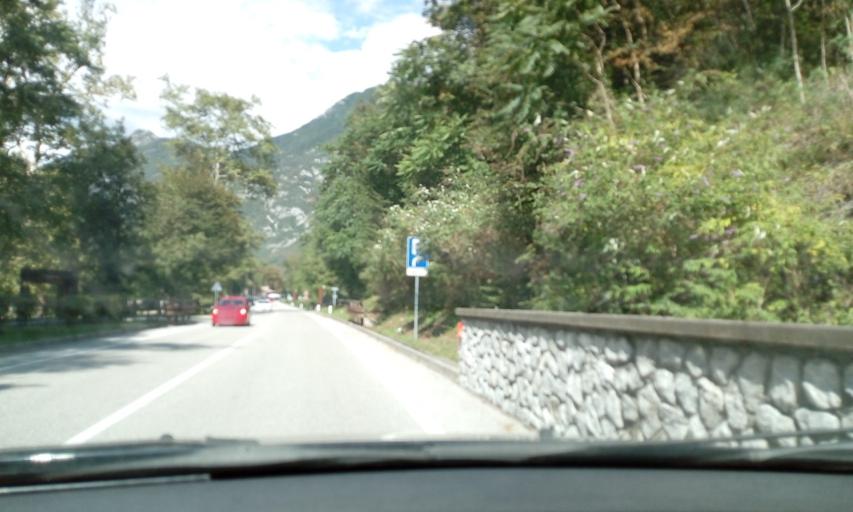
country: IT
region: Friuli Venezia Giulia
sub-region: Provincia di Udine
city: Trasaghis
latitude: 46.3181
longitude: 13.0681
